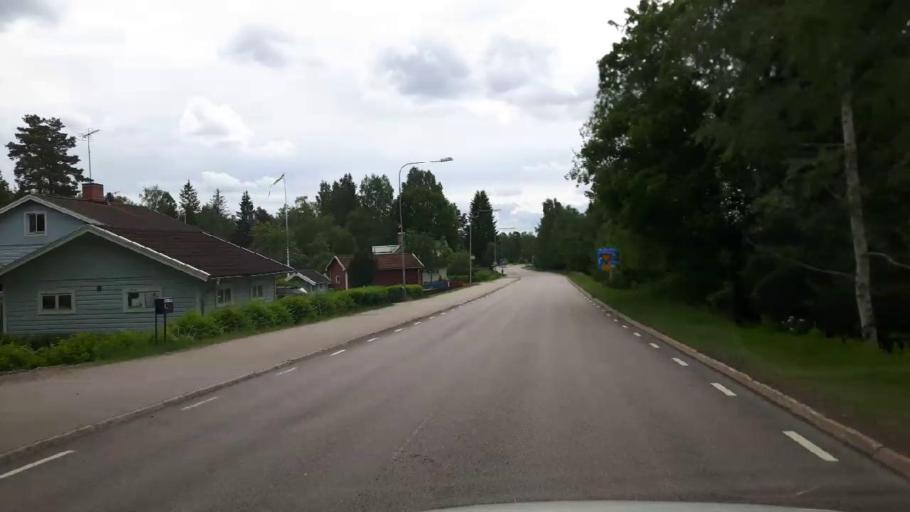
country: SE
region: Vaestmanland
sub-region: Norbergs Kommun
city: Norberg
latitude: 60.0770
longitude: 15.9305
